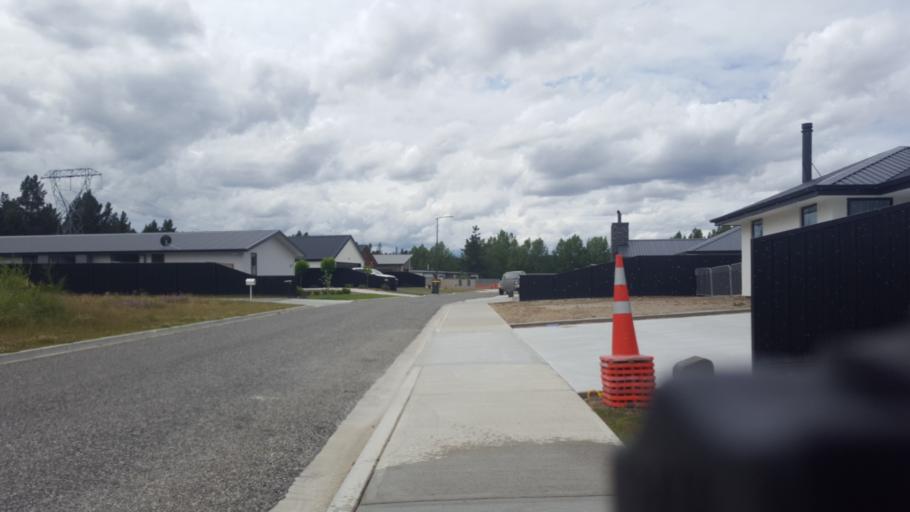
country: NZ
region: Otago
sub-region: Queenstown-Lakes District
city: Wanaka
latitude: -45.2429
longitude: 169.3750
